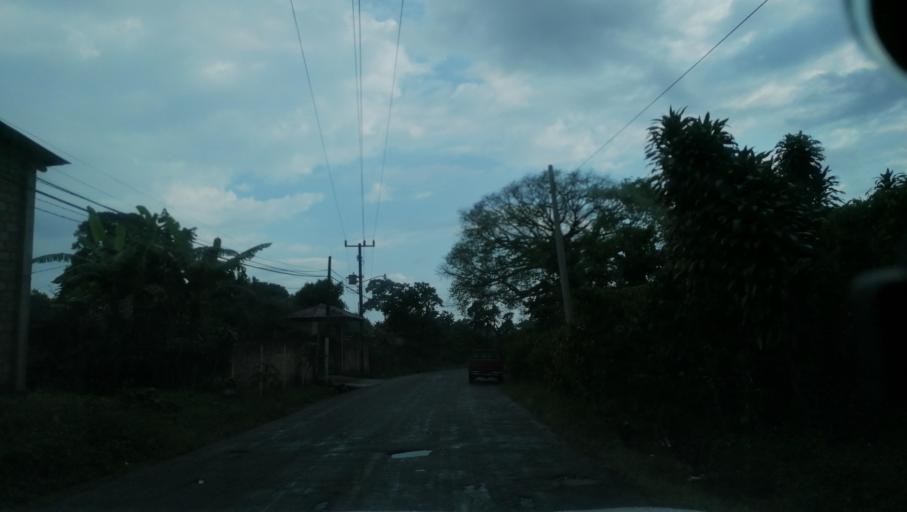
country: MX
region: Chiapas
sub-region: Cacahoatan
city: Benito Juarez
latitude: 15.0470
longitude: -92.1866
